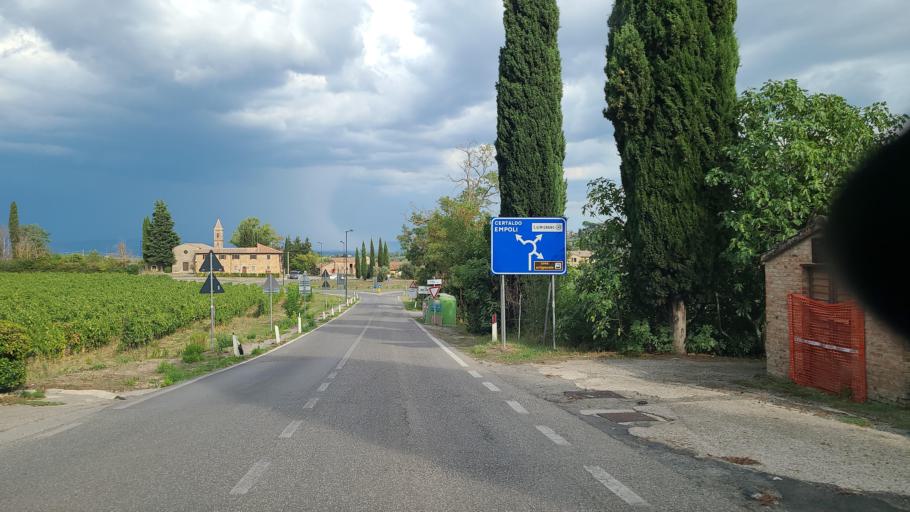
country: IT
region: Tuscany
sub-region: Provincia di Siena
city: San Gimignano
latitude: 43.4768
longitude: 11.0272
